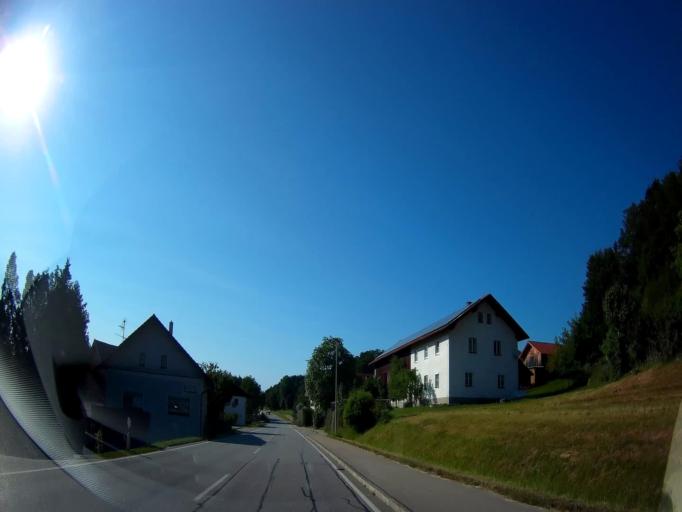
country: DE
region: Bavaria
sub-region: Upper Bavaria
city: Marktl
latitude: 48.2833
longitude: 12.8653
